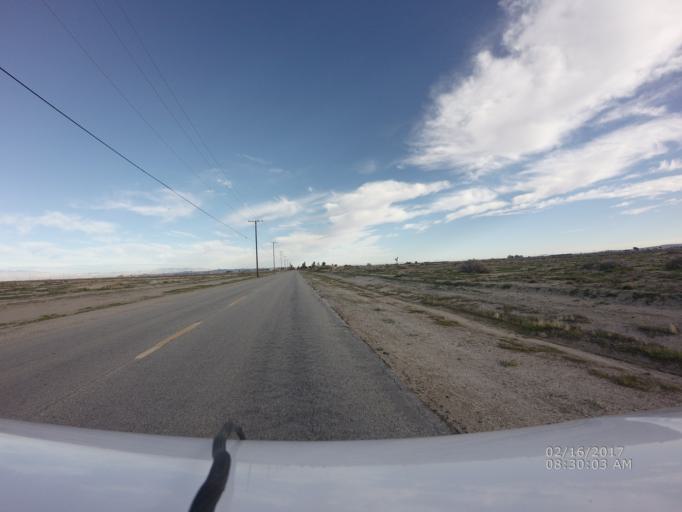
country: US
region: California
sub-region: Los Angeles County
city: Lancaster
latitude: 34.6996
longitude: -118.0054
